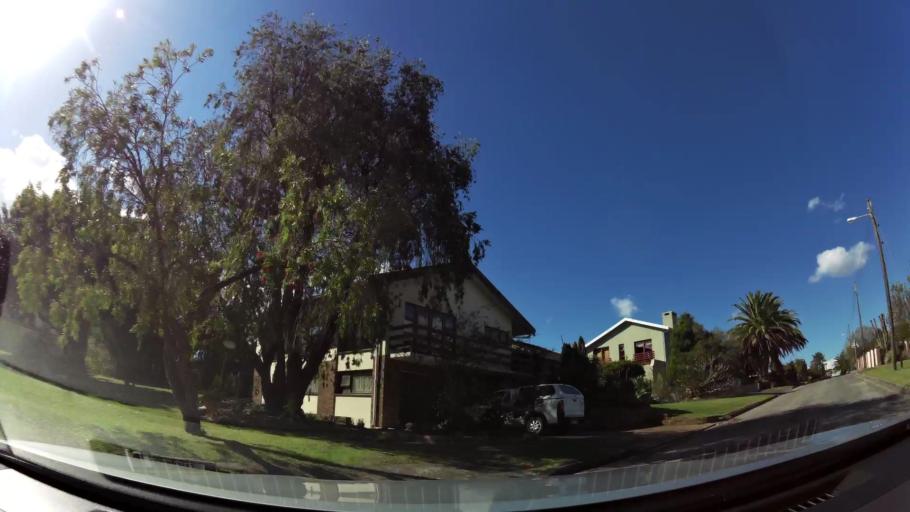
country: ZA
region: Western Cape
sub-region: Eden District Municipality
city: George
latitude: -33.9603
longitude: 22.4490
